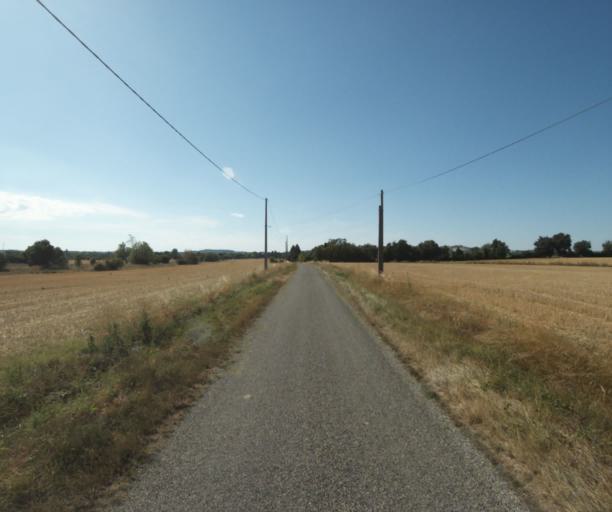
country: FR
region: Midi-Pyrenees
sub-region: Departement de la Haute-Garonne
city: Revel
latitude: 43.4713
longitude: 1.9683
